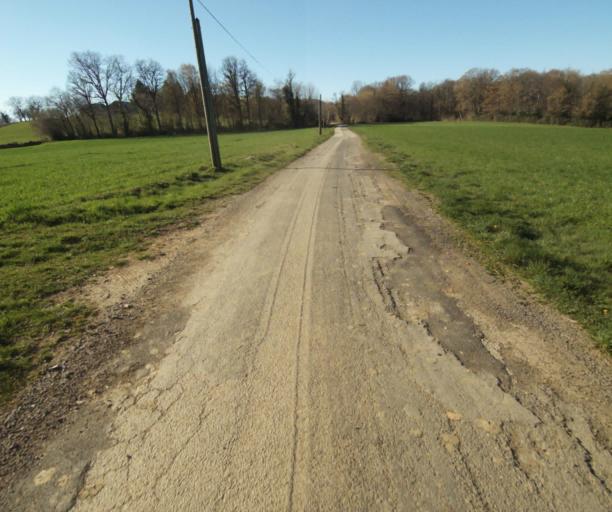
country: FR
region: Limousin
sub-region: Departement de la Correze
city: Seilhac
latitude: 45.3871
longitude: 1.7341
